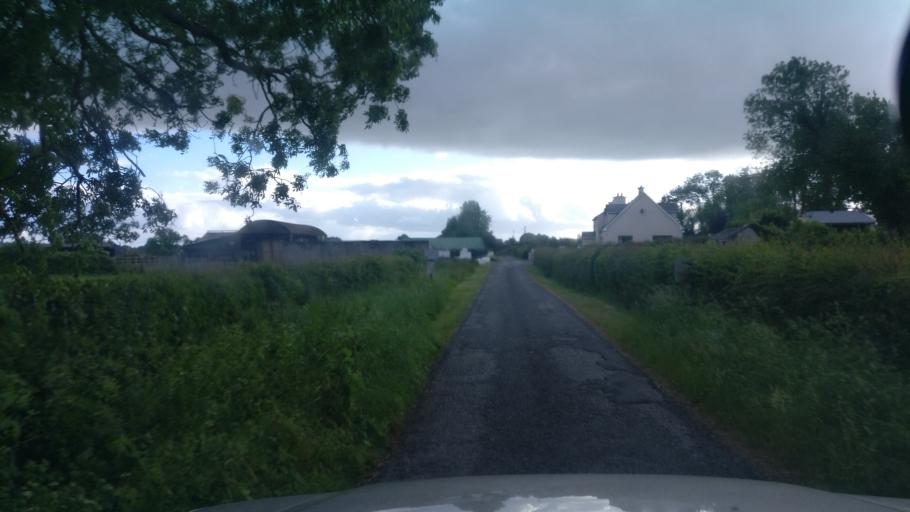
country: IE
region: Connaught
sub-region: County Galway
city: Ballinasloe
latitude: 53.2303
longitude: -8.2199
